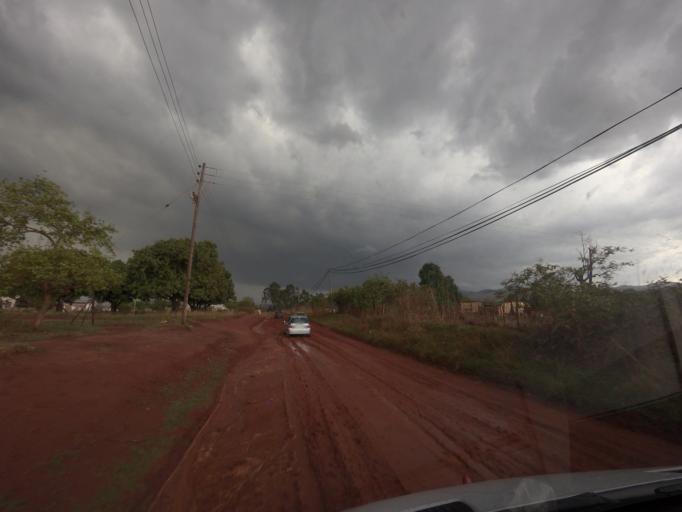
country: SZ
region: Hhohho
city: Lobamba
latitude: -26.4672
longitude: 31.2113
